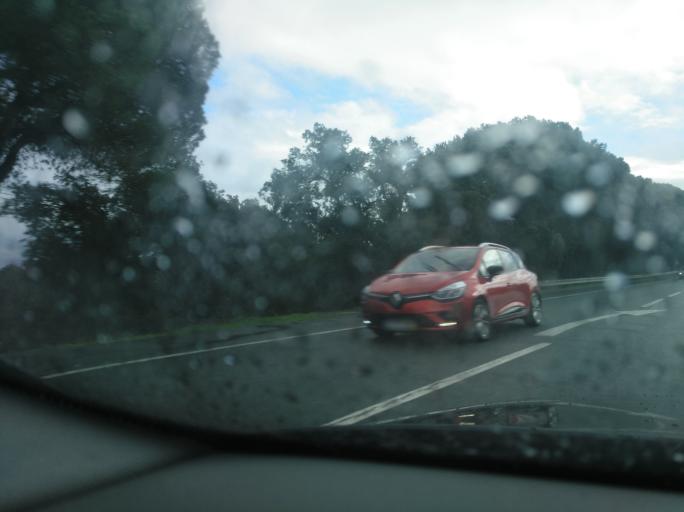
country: PT
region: Setubal
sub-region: Grandola
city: Grandola
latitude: 38.0827
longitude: -8.4173
